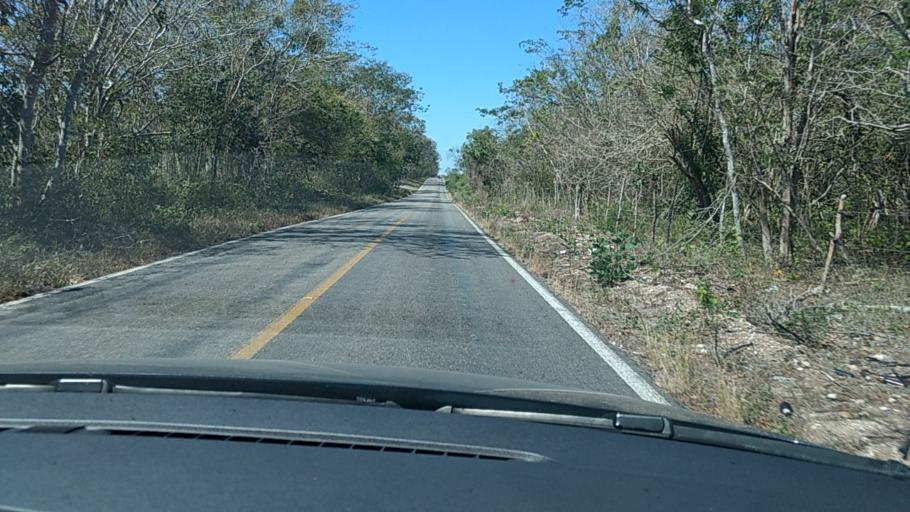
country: MX
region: Yucatan
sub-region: Tizimin
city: Tizimin
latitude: 21.1989
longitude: -88.1843
